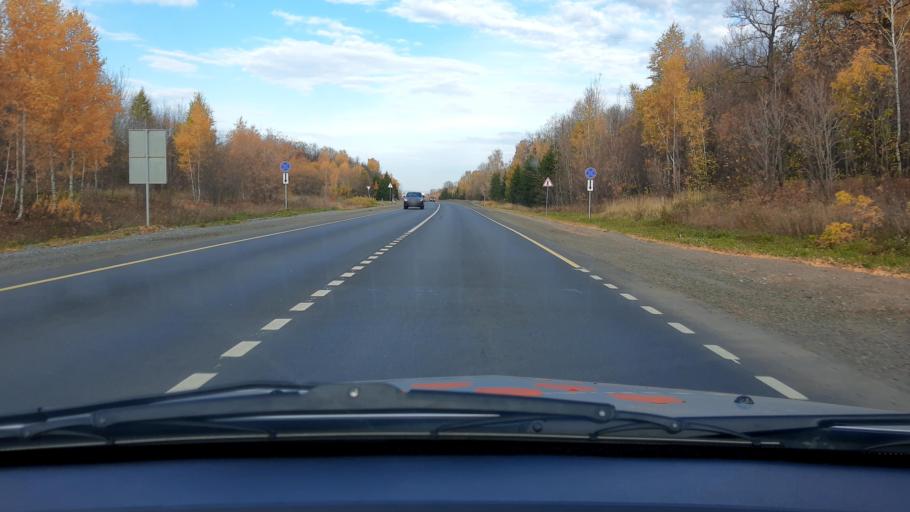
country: RU
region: Bashkortostan
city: Avdon
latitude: 54.8354
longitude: 55.7226
